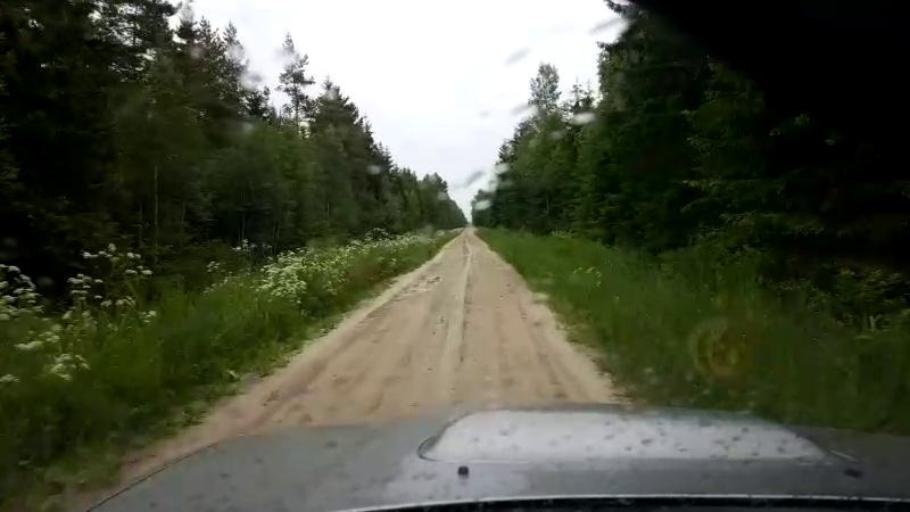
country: EE
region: Paernumaa
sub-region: Halinga vald
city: Parnu-Jaagupi
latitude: 58.5863
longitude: 24.6350
